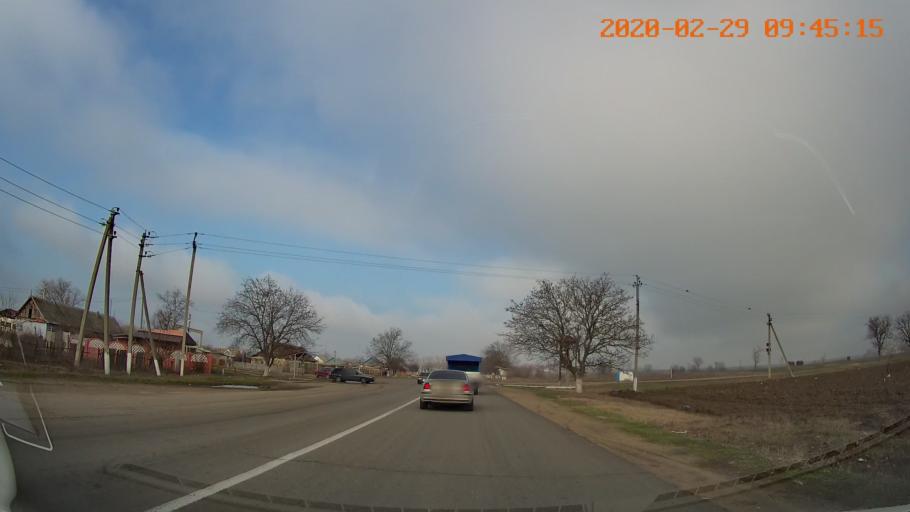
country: MD
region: Telenesti
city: Crasnoe
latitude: 46.6589
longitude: 29.8112
